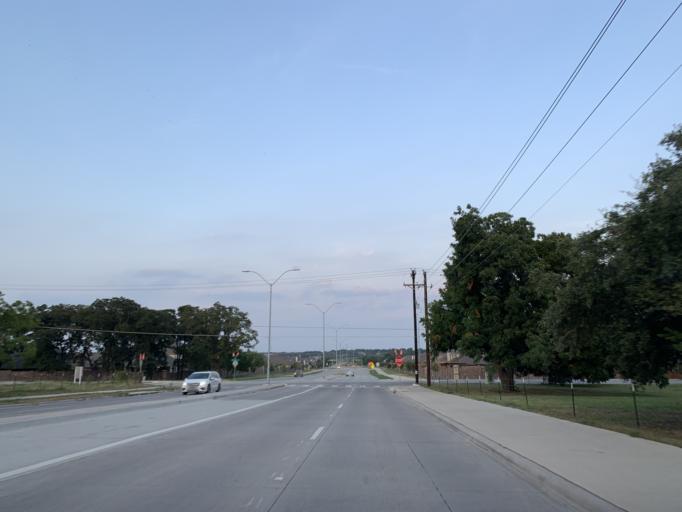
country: US
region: Texas
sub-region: Tarrant County
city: Keller
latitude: 32.9554
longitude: -97.2704
